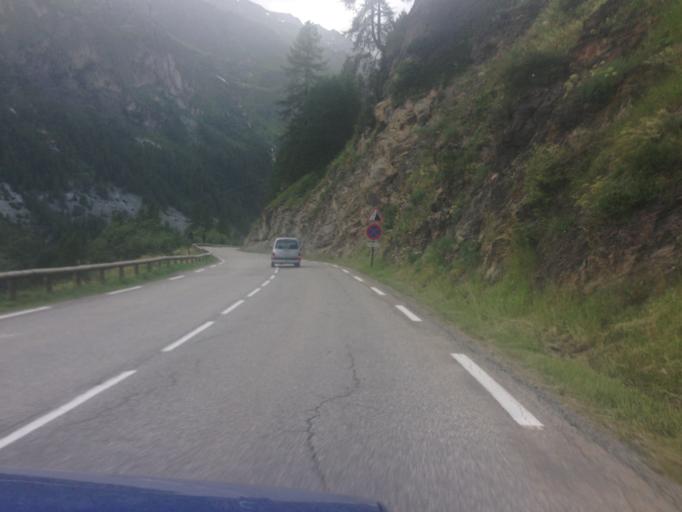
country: FR
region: Rhone-Alpes
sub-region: Departement de la Savoie
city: Tignes
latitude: 45.5096
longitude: 6.9241
